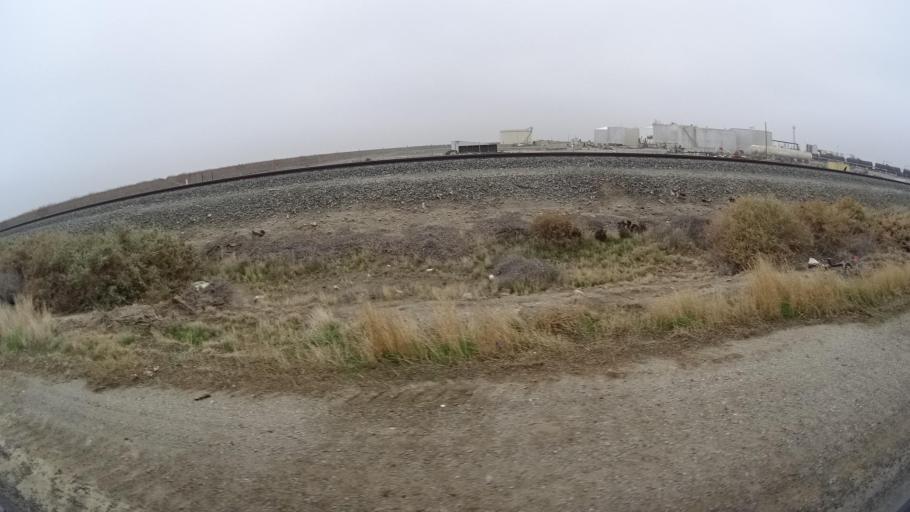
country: US
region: California
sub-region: Kern County
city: Greenfield
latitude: 35.1802
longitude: -119.1576
